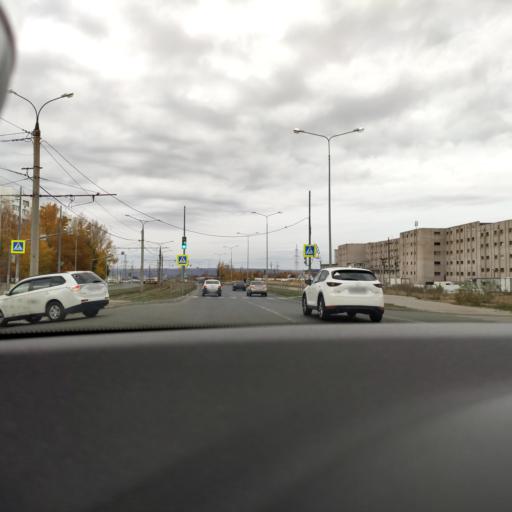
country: RU
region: Samara
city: Samara
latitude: 53.2657
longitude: 50.2311
